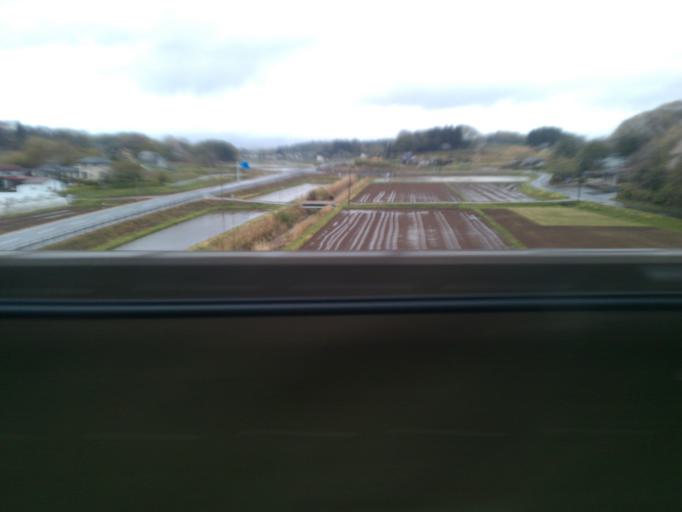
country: JP
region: Fukushima
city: Sukagawa
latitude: 37.2764
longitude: 140.3217
